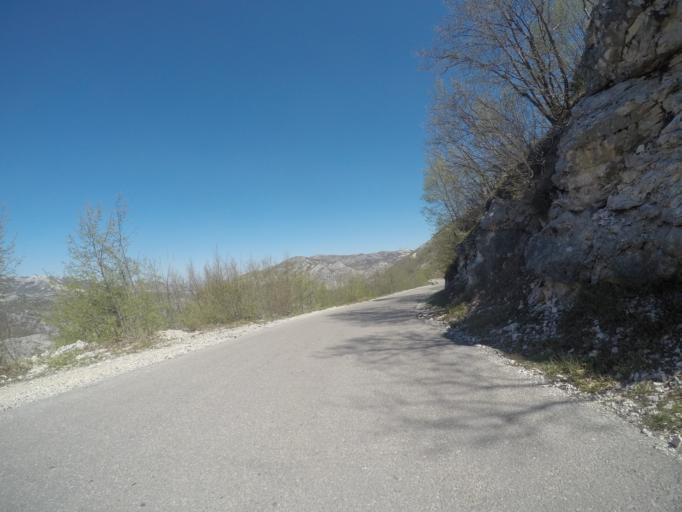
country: ME
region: Cetinje
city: Cetinje
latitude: 42.4473
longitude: 18.8730
